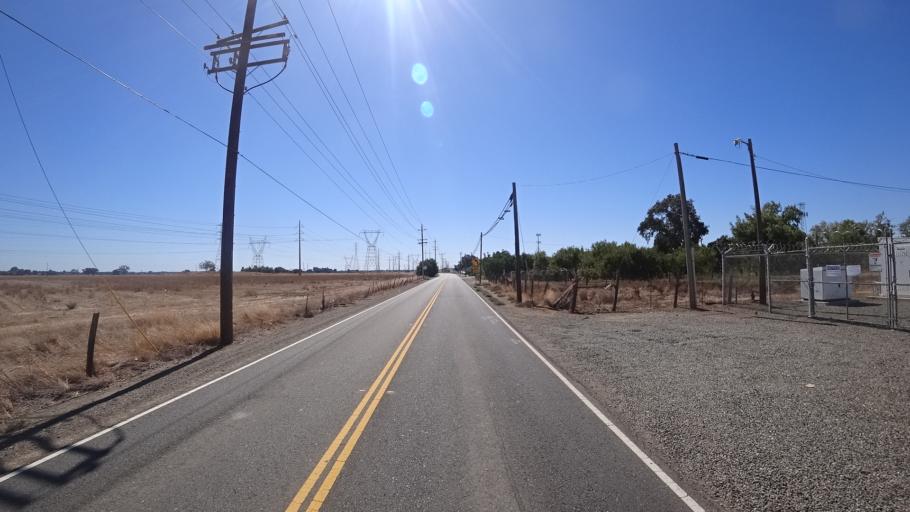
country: US
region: California
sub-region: Sacramento County
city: Elk Grove
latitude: 38.3903
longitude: -121.3529
